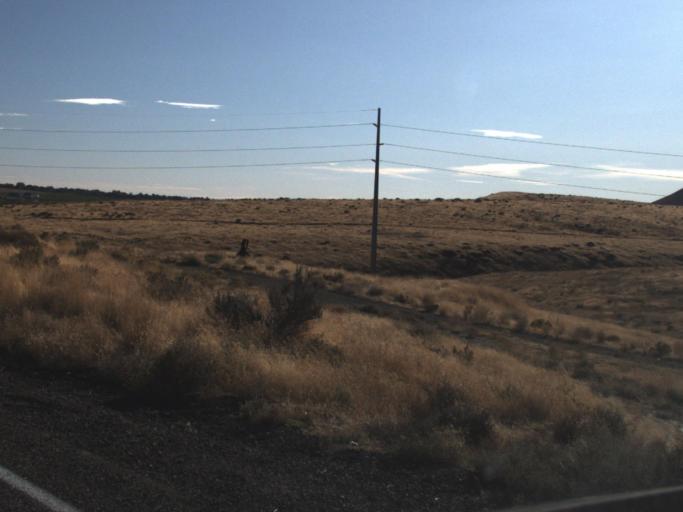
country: US
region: Washington
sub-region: Benton County
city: West Richland
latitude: 46.2769
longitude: -119.4070
